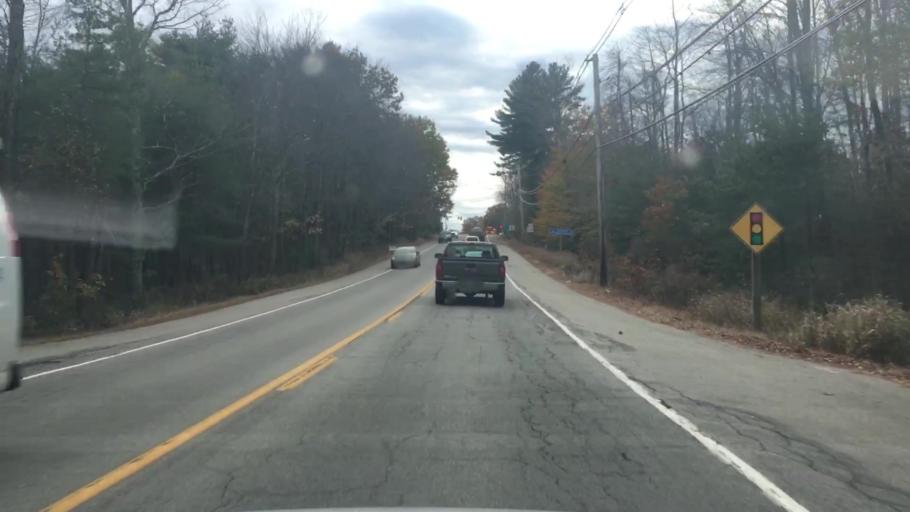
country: US
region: Maine
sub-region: York County
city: Sanford (historical)
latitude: 43.4612
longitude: -70.7595
